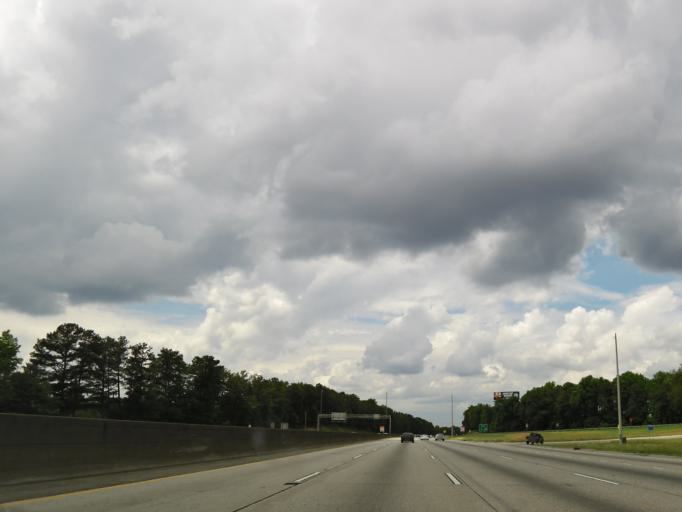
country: US
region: Georgia
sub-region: Fulton County
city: College Park
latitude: 33.6372
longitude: -84.4926
